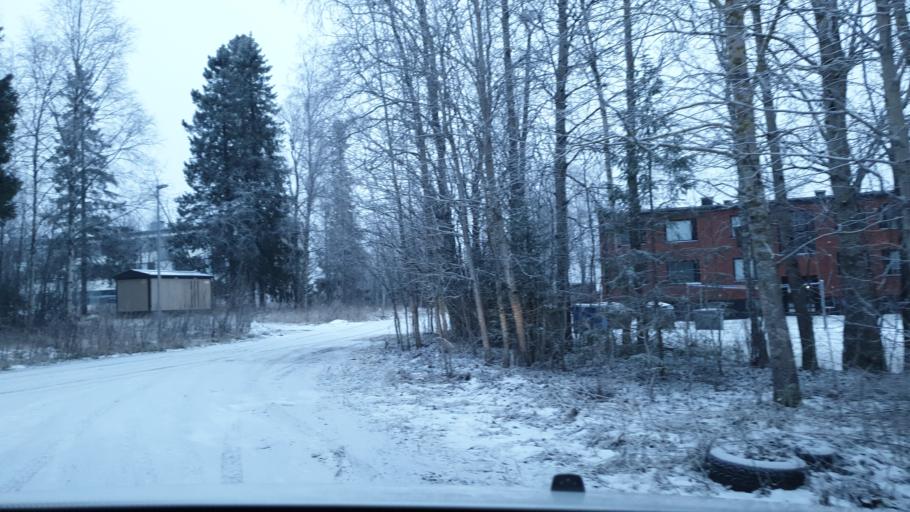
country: FI
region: Lapland
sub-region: Kemi-Tornio
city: Kemi
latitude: 65.7324
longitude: 24.5992
